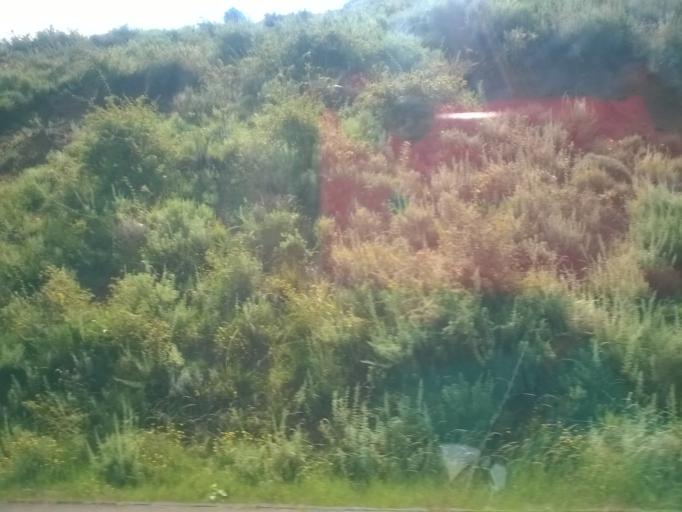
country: LS
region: Thaba-Tseka
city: Thaba-Tseka
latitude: -29.1395
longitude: 28.4911
